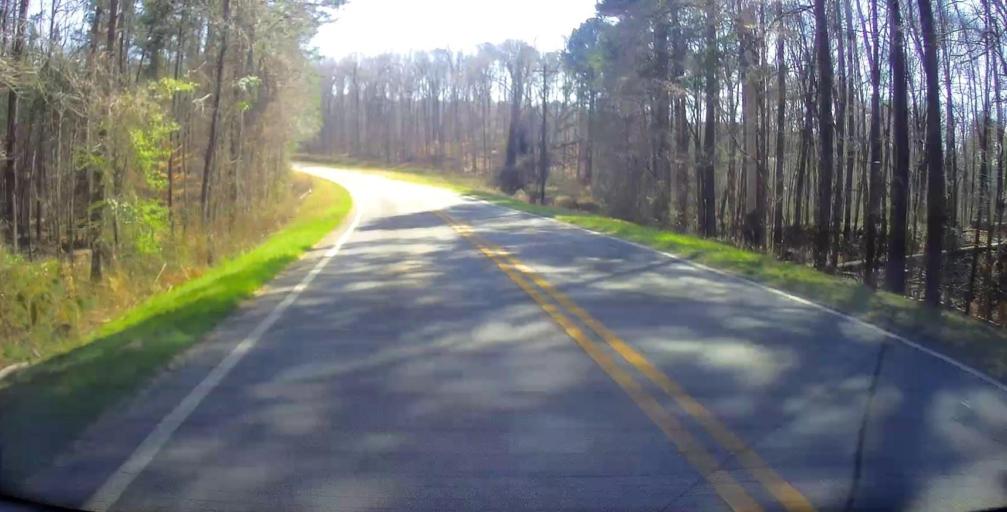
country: US
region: Georgia
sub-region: Jones County
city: Gray
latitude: 32.9500
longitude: -83.5438
